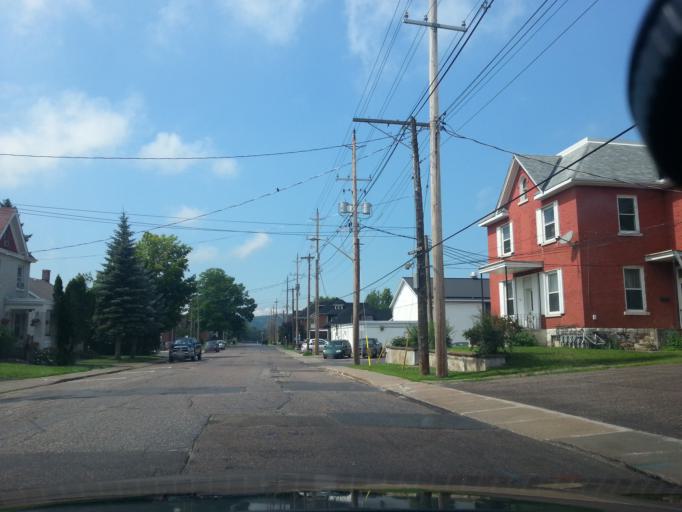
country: CA
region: Ontario
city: Renfrew
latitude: 45.4734
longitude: -76.6873
